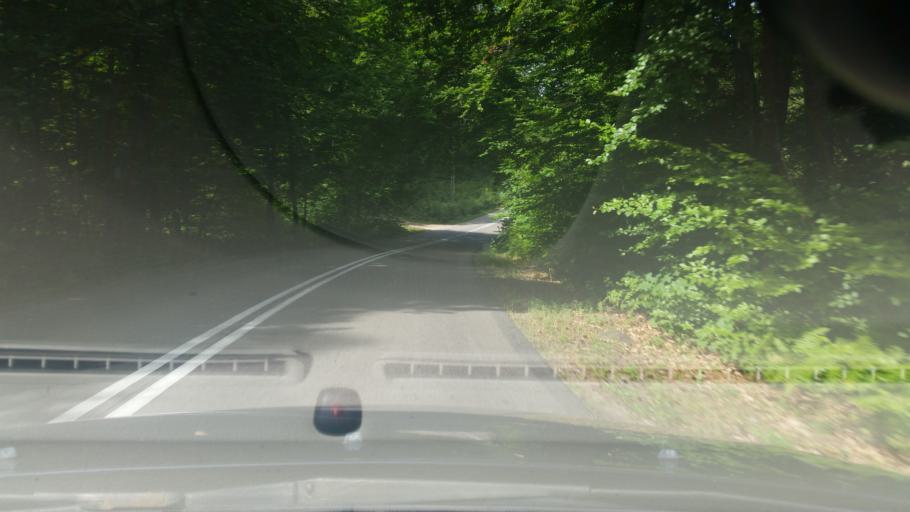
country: PL
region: Pomeranian Voivodeship
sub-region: Powiat wejherowski
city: Choczewo
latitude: 54.7459
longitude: 17.7369
